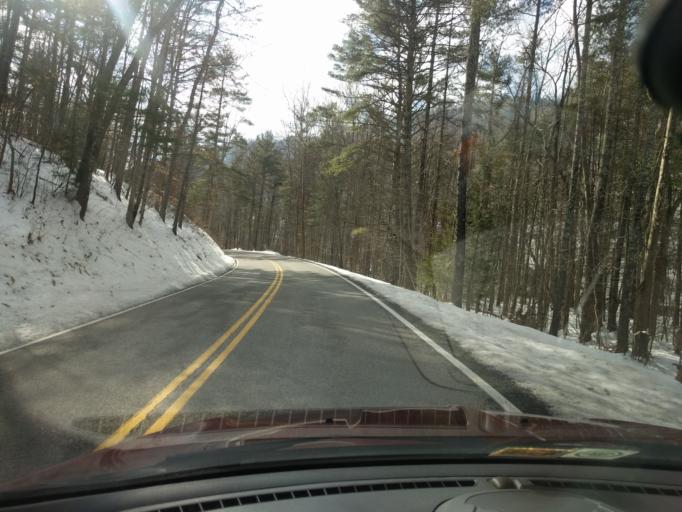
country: US
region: Virginia
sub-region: Bath County
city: Warm Springs
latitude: 38.1171
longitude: -79.9147
